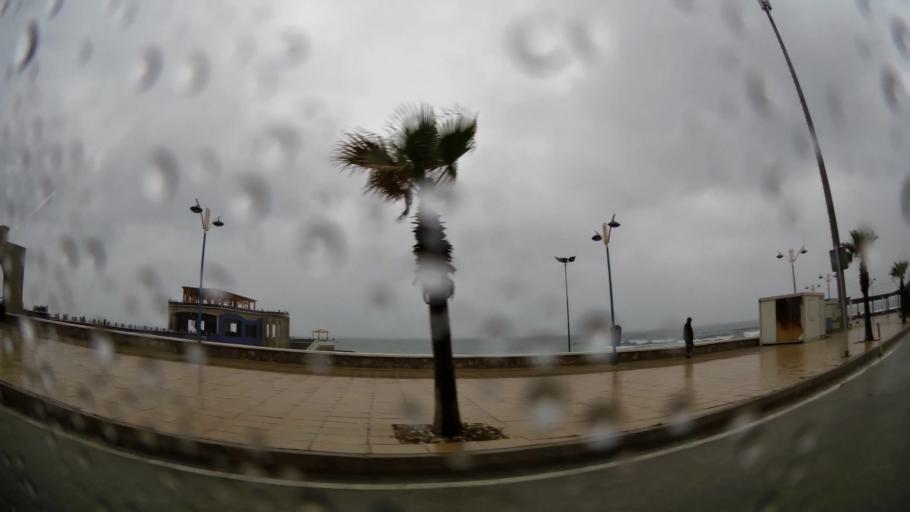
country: MA
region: Taza-Al Hoceima-Taounate
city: Tirhanimine
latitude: 35.2478
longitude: -3.9573
